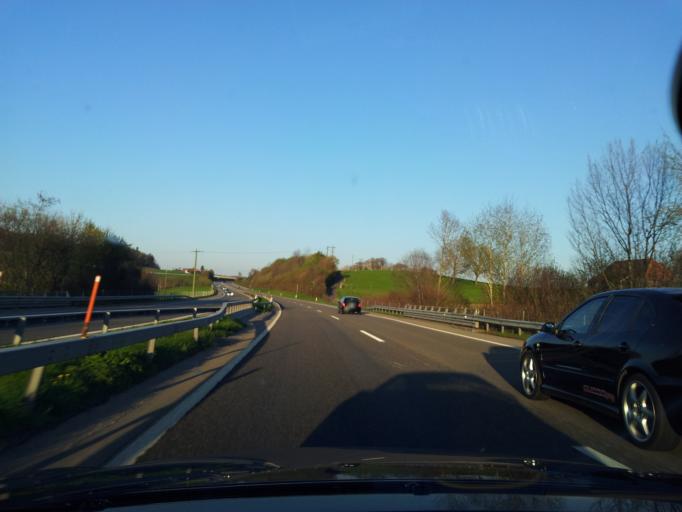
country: CH
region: Bern
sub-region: Seeland District
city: Grossaffoltern
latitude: 47.0481
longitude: 7.3515
